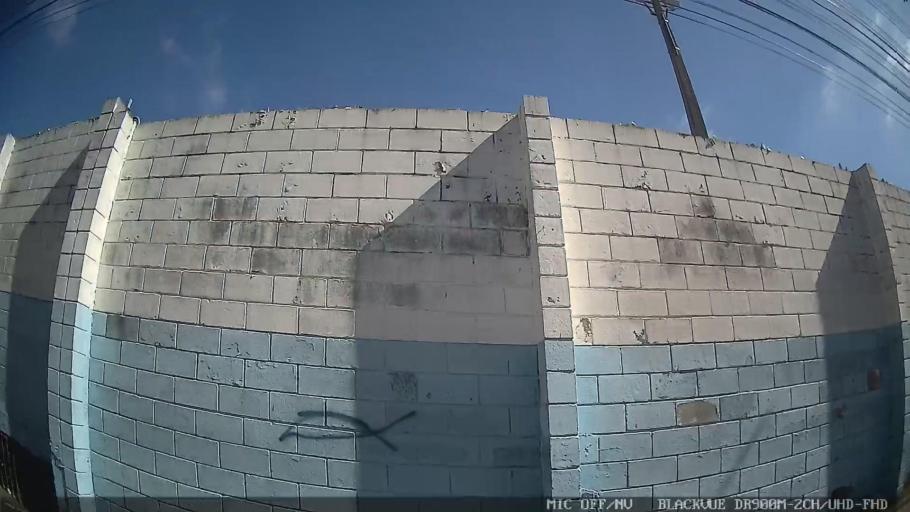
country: BR
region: Sao Paulo
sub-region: Poa
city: Poa
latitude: -23.5079
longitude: -46.3403
